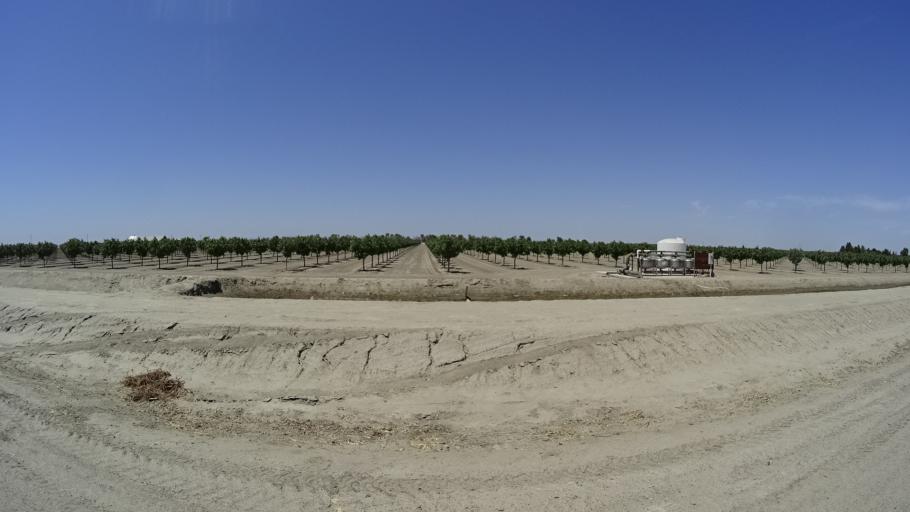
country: US
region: California
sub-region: Kings County
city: Corcoran
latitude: 36.1124
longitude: -119.6257
